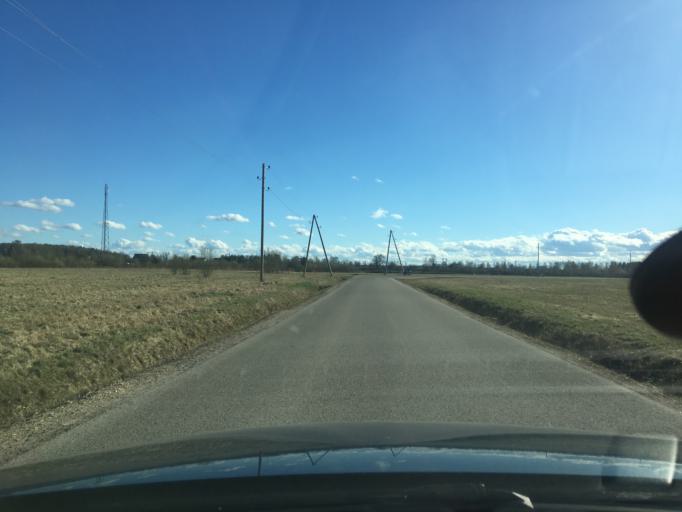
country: LV
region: Salaspils
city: Salaspils
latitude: 56.8691
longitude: 24.3229
